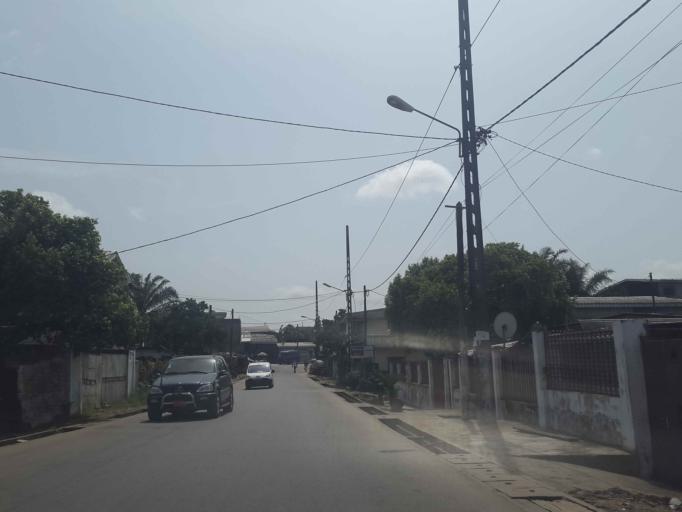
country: CM
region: Littoral
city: Douala
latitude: 4.0716
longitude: 9.7162
